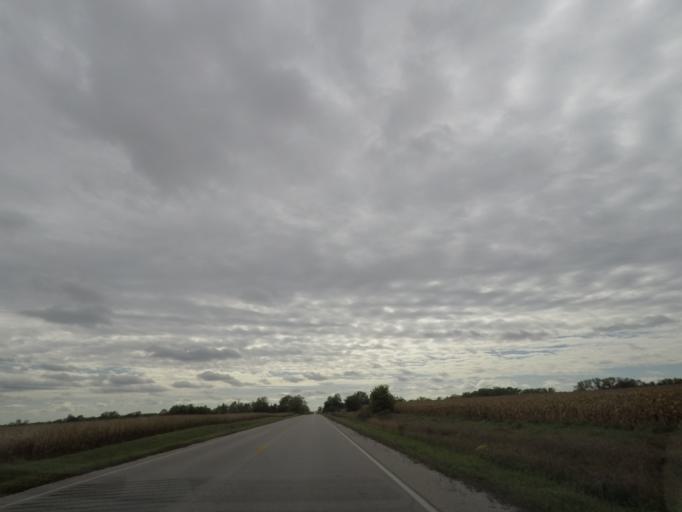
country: US
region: Iowa
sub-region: Story County
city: Huxley
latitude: 41.8738
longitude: -93.5315
